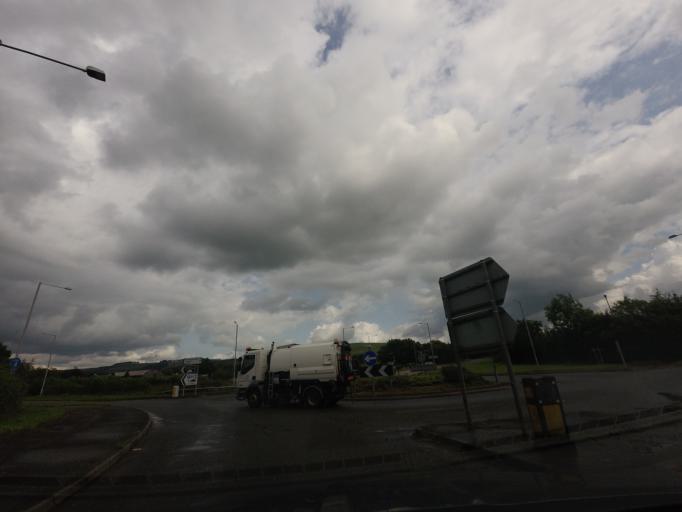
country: GB
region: Scotland
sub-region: Dumfries and Galloway
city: Lockerbie
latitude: 55.1337
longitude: -3.3641
